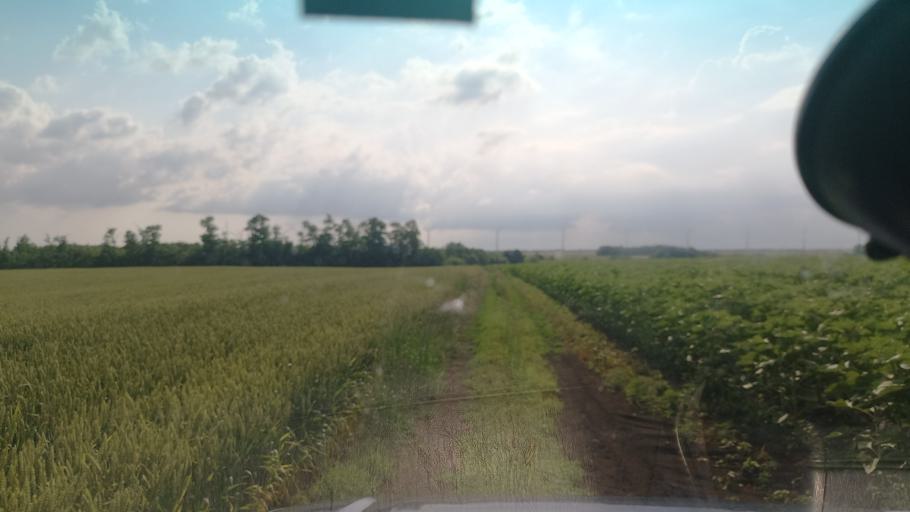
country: RU
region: Adygeya
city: Giaginskaya
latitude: 44.9570
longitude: 40.1113
